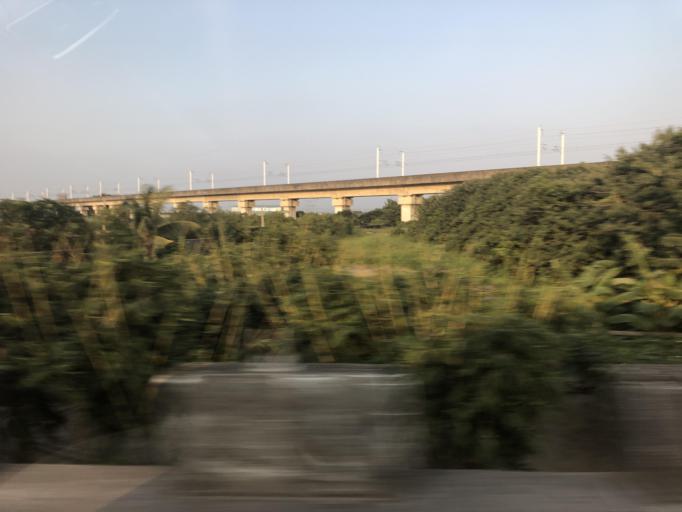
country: TW
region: Taiwan
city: Xinying
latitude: 23.1549
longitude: 120.2769
